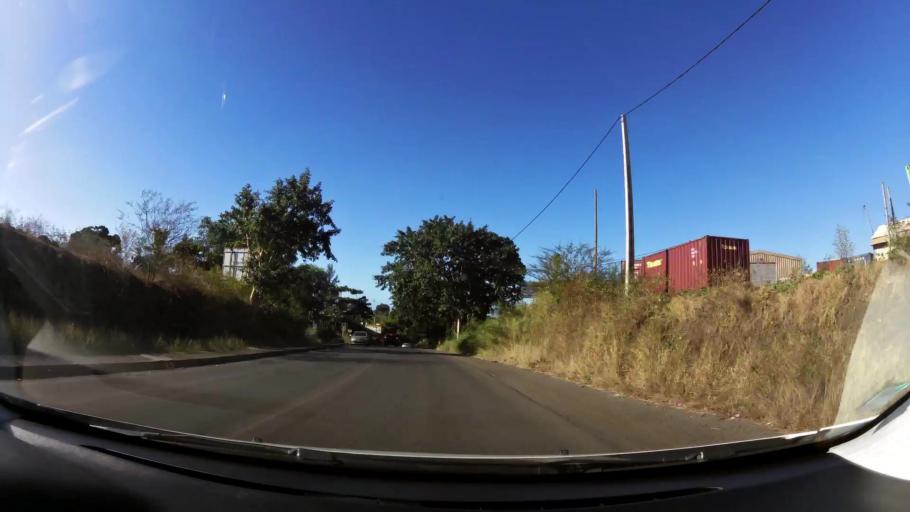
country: YT
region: Mamoudzou
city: Mamoudzou
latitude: -12.7590
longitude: 45.2307
